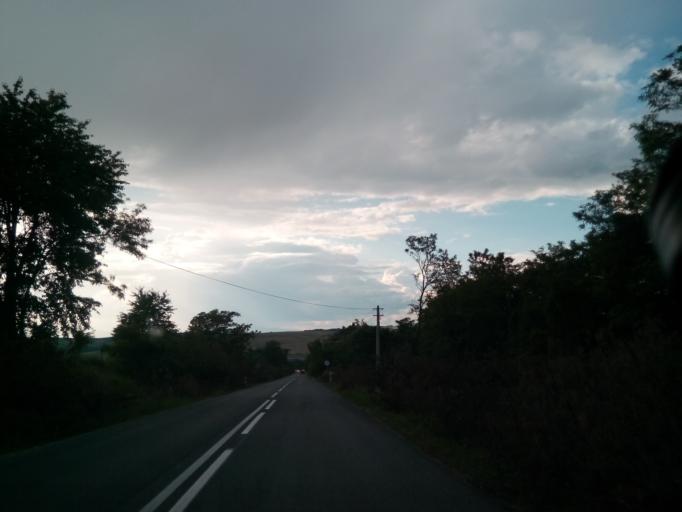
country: SK
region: Kosicky
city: Kosice
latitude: 48.6484
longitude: 21.4108
